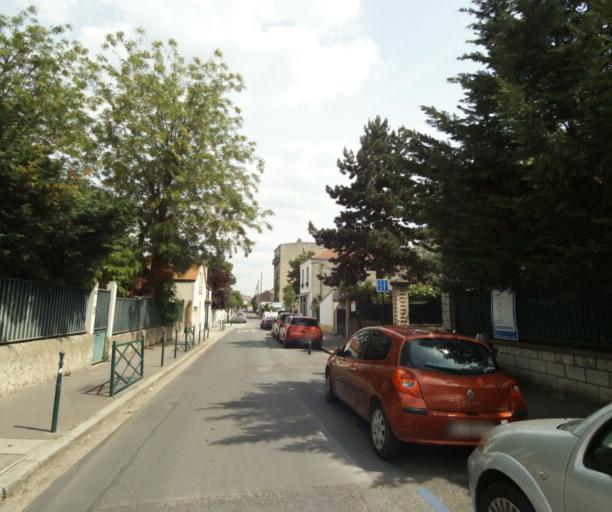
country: FR
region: Ile-de-France
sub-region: Departement des Hauts-de-Seine
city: Colombes
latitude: 48.9177
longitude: 2.2590
